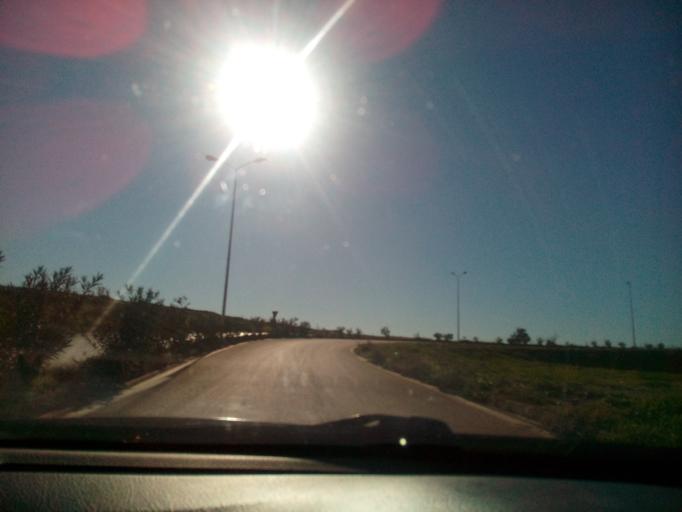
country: DZ
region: Relizane
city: Relizane
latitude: 35.7110
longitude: 0.5302
